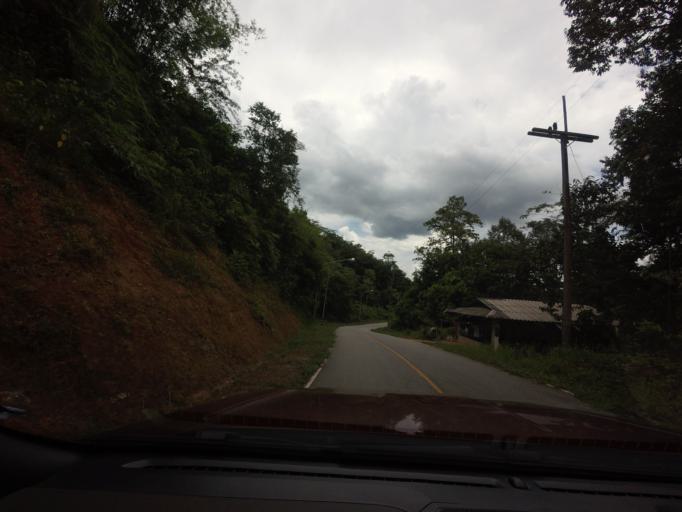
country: TH
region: Narathiwat
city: Sukhirin
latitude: 5.9917
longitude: 101.7040
